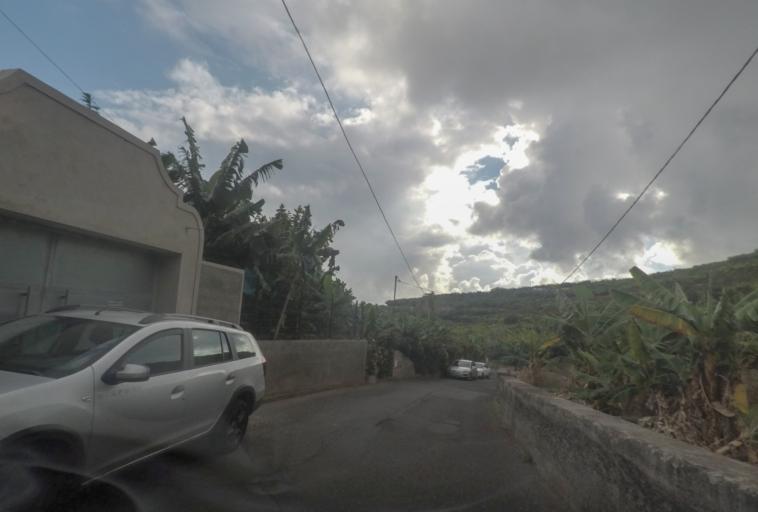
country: PT
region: Madeira
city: Camara de Lobos
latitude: 32.6564
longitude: -16.9587
